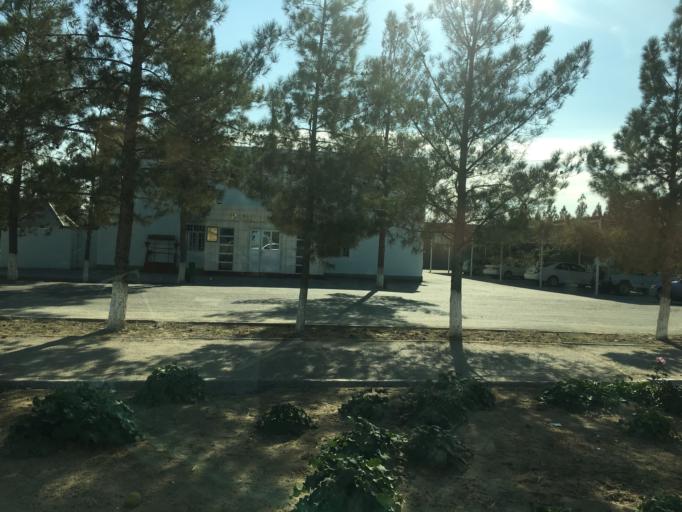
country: TM
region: Mary
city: Mary
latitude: 37.5980
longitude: 61.5892
